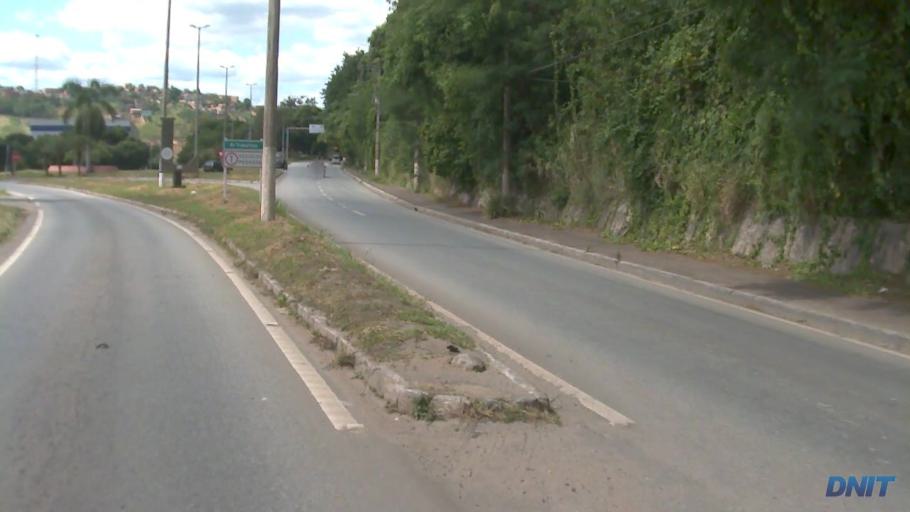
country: BR
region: Minas Gerais
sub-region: Coronel Fabriciano
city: Coronel Fabriciano
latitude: -19.5280
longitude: -42.6427
